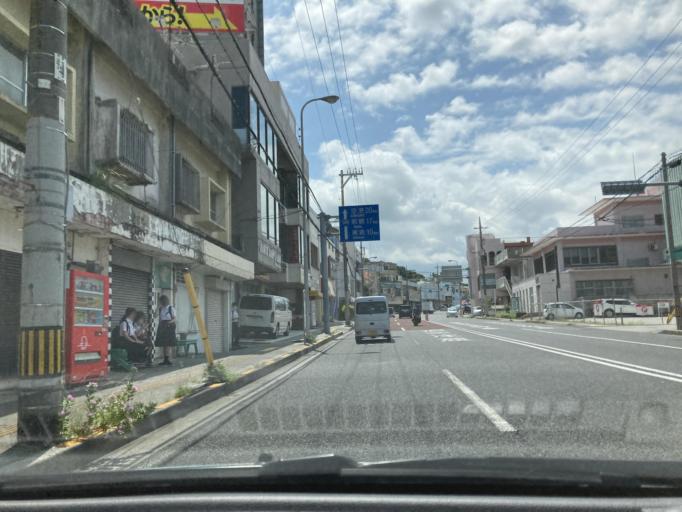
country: JP
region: Okinawa
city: Chatan
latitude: 26.2889
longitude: 127.7779
